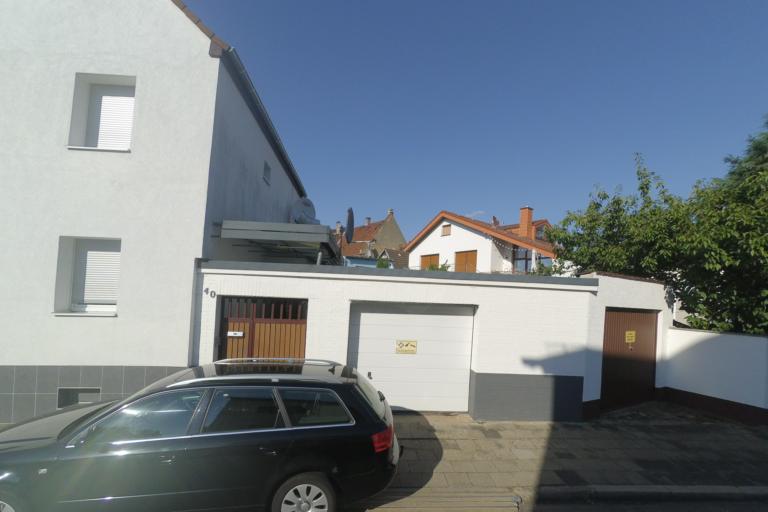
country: DE
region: Hesse
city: Lampertheim
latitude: 49.5939
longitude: 8.4732
